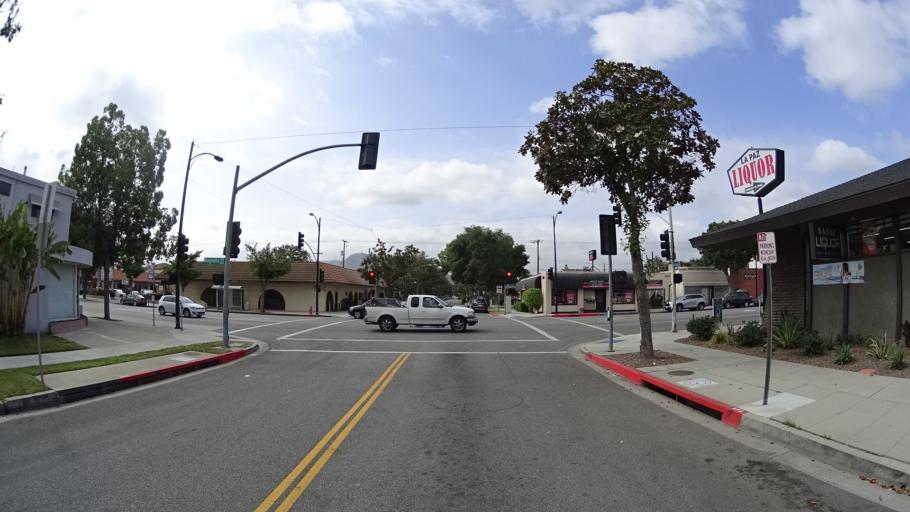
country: US
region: California
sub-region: Los Angeles County
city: Universal City
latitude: 34.1668
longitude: -118.3511
